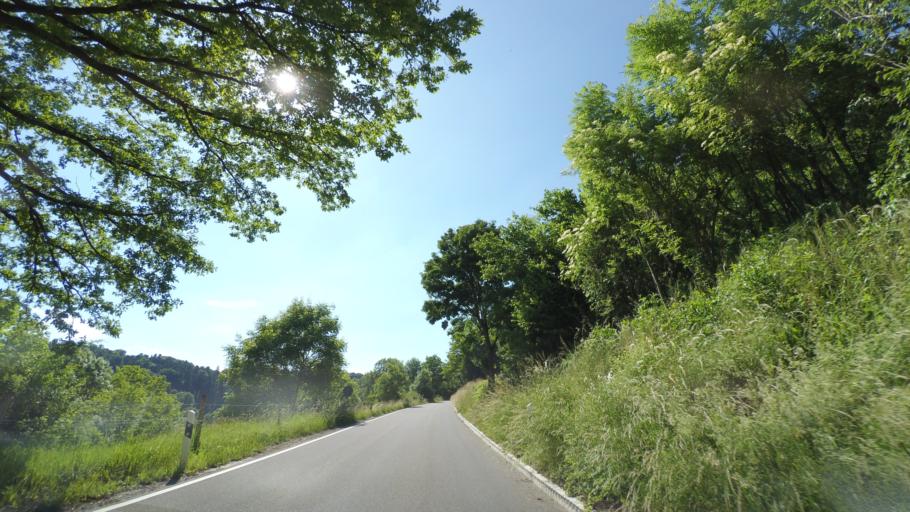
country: DE
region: Baden-Wuerttemberg
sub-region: Regierungsbezirk Stuttgart
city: Wolpertshausen
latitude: 49.1420
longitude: 9.8476
